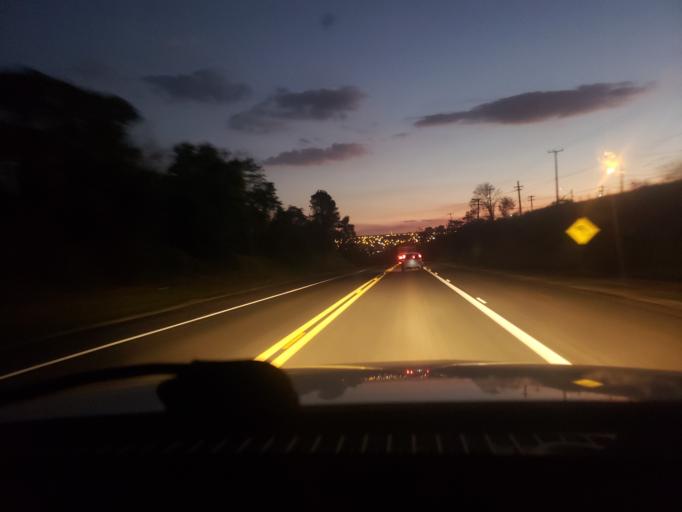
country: BR
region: Sao Paulo
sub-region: Conchal
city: Conchal
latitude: -22.3315
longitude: -47.1531
